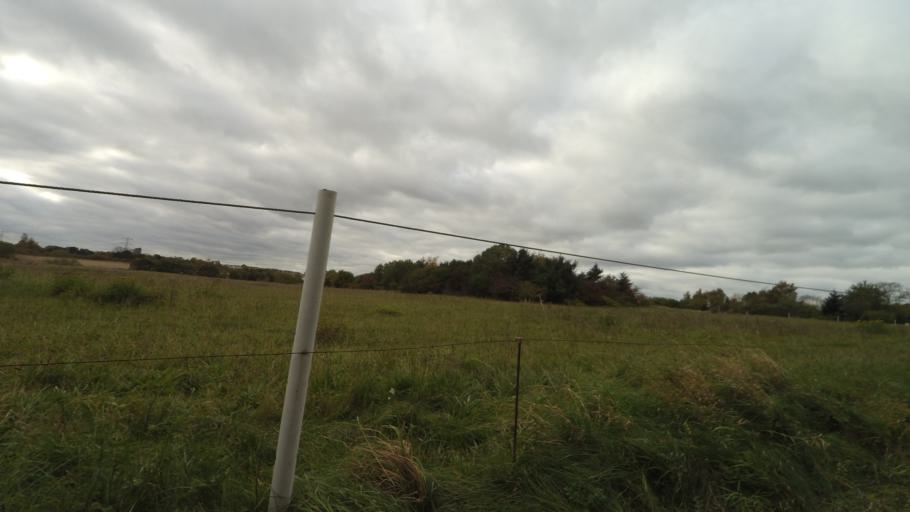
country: DK
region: Central Jutland
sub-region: Arhus Kommune
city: Kolt
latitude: 56.1435
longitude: 10.0593
